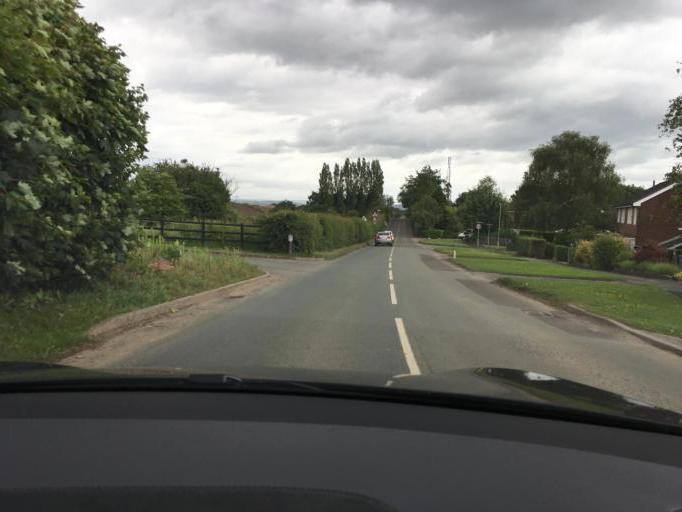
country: GB
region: England
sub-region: Borough of Stockport
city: Bramhall
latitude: 53.3530
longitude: -2.1439
